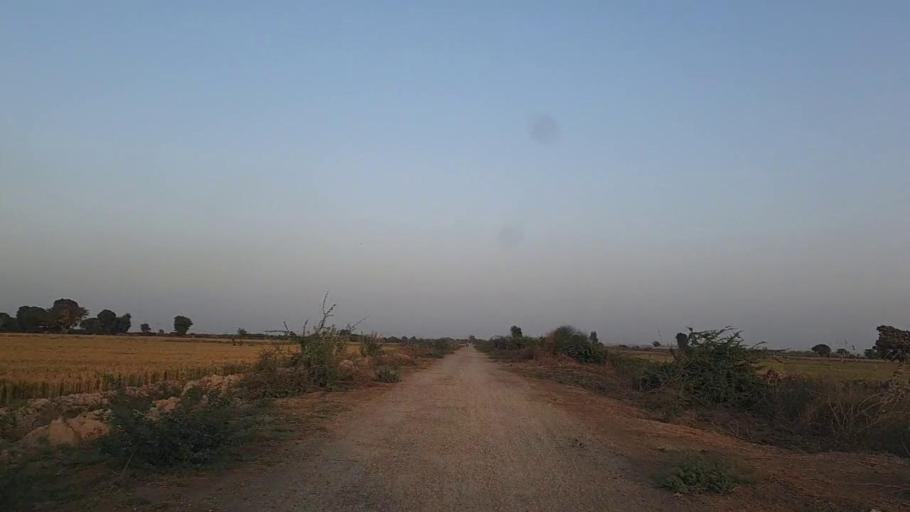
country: PK
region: Sindh
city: Naukot
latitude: 24.6953
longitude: 69.2777
